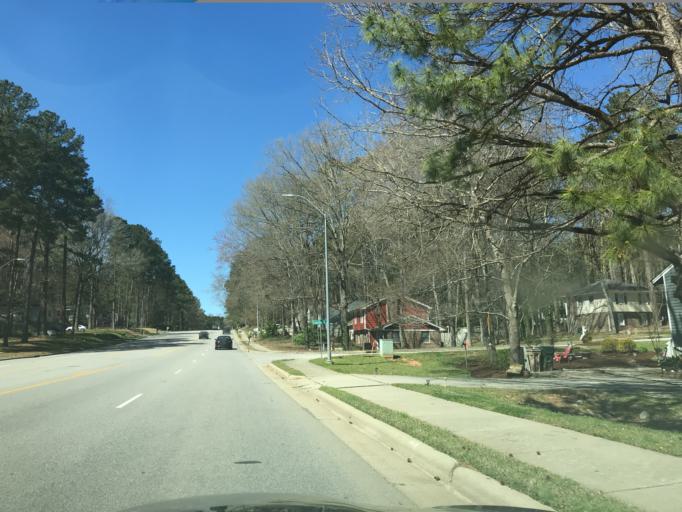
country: US
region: North Carolina
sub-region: Wake County
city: Garner
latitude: 35.6859
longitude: -78.6246
